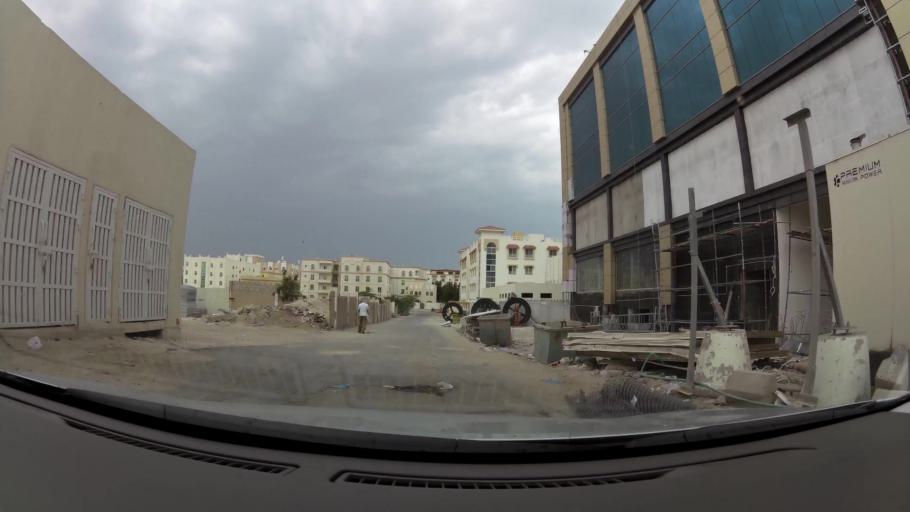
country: QA
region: Baladiyat ad Dawhah
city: Doha
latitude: 25.2738
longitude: 51.4965
